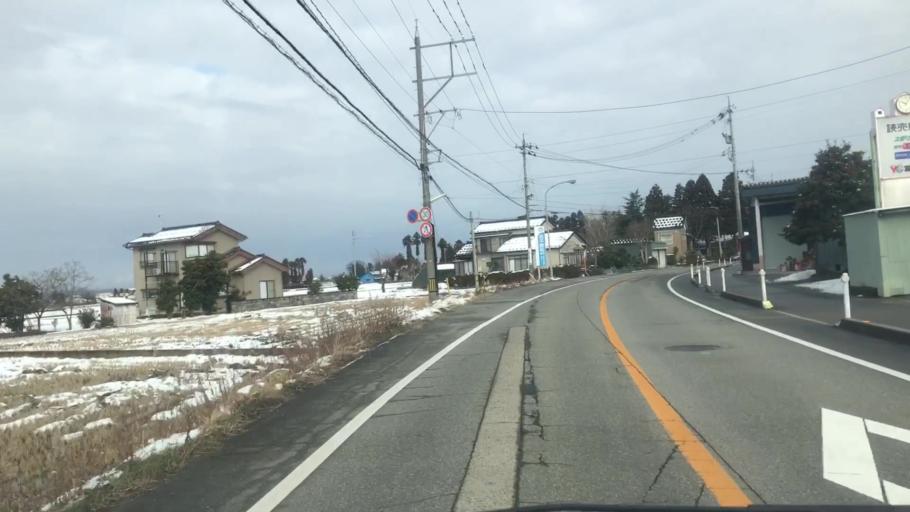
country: JP
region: Toyama
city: Toyama-shi
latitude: 36.6181
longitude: 137.2513
